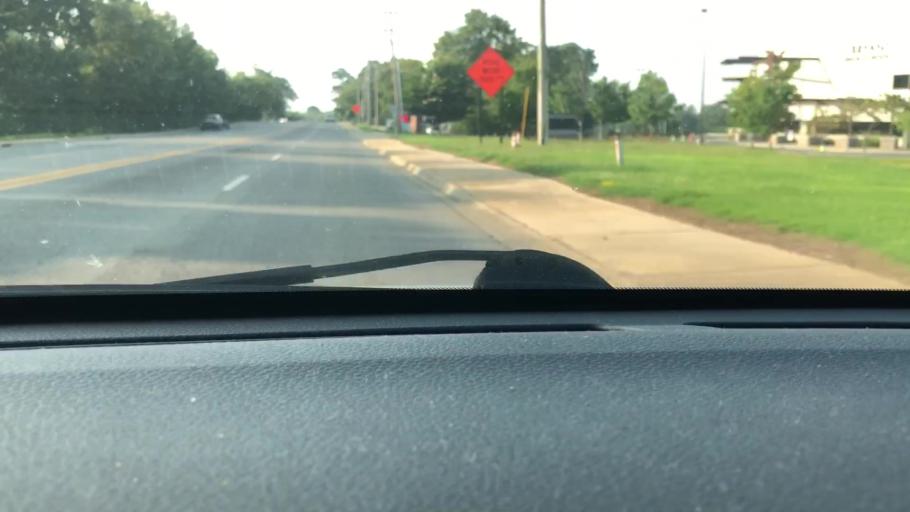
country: US
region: Arkansas
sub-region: Saline County
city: Bryant
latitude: 34.6023
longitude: -92.4905
